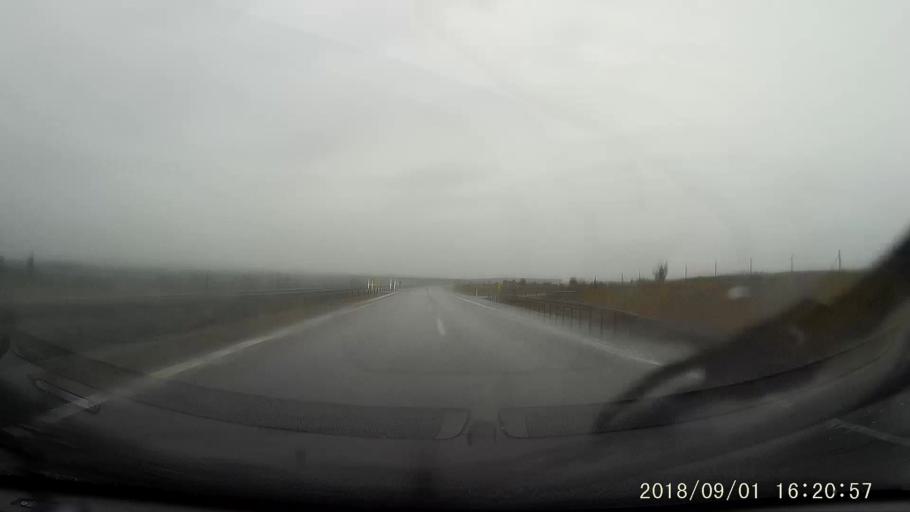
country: PL
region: Lubusz
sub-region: Powiat miedzyrzecki
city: Miedzyrzecz
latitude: 52.3529
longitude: 15.5551
